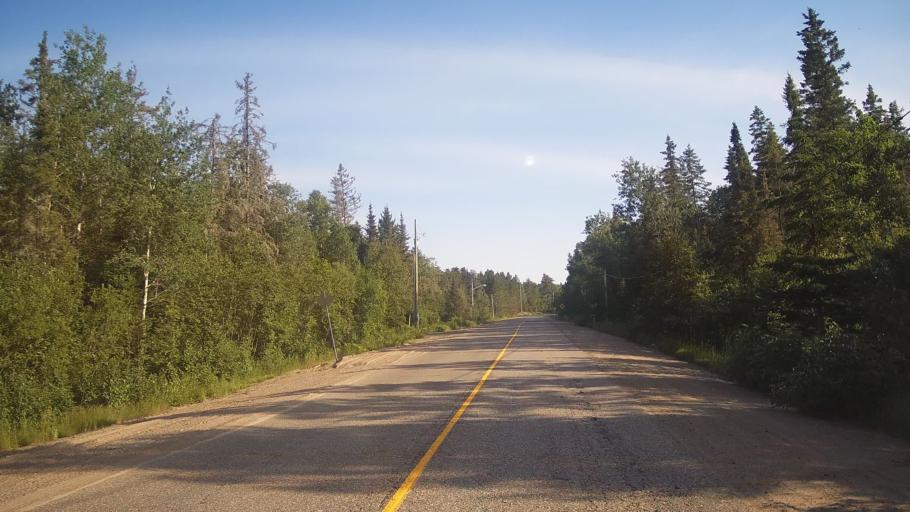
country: CA
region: Ontario
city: Rayside-Balfour
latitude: 46.5772
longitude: -81.3081
